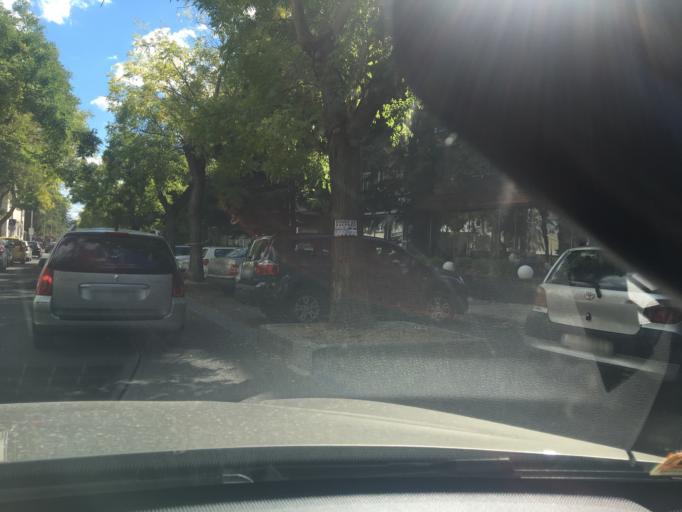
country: BG
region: Burgas
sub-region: Obshtina Burgas
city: Burgas
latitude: 42.5011
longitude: 27.4709
